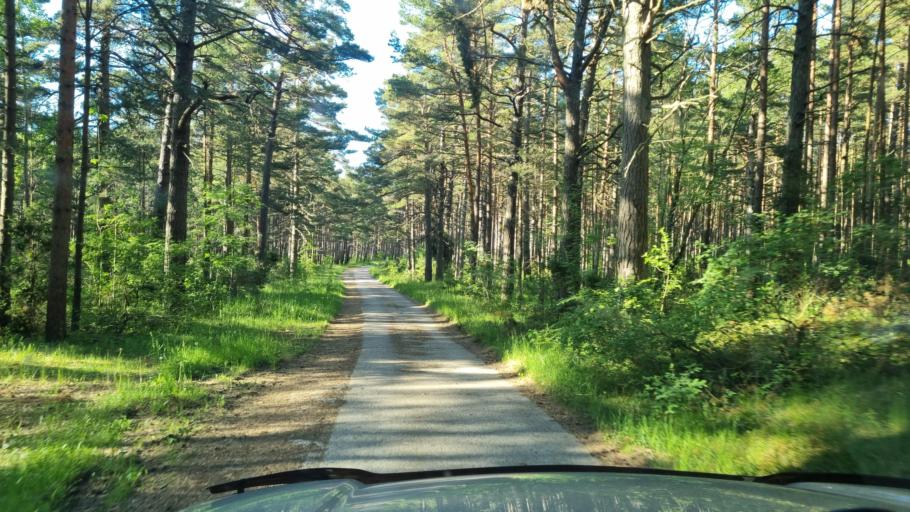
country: LV
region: Ventspils
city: Ventspils
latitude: 57.3694
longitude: 21.5202
